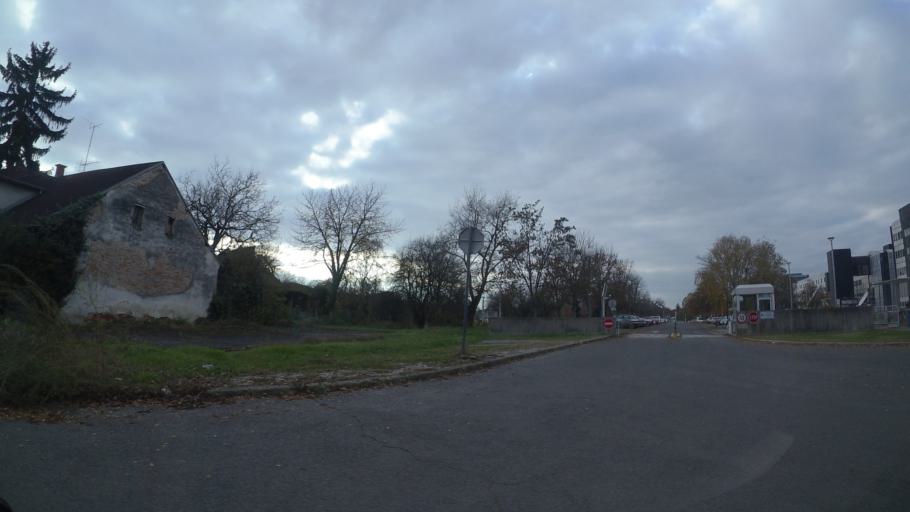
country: HR
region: Grad Zagreb
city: Novi Zagreb
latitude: 45.7921
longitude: 15.9758
